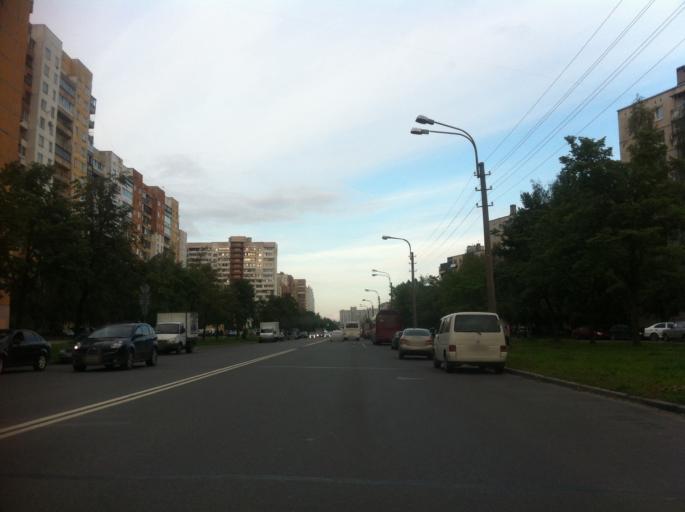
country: RU
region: St.-Petersburg
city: Uritsk
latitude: 59.8518
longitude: 30.2018
